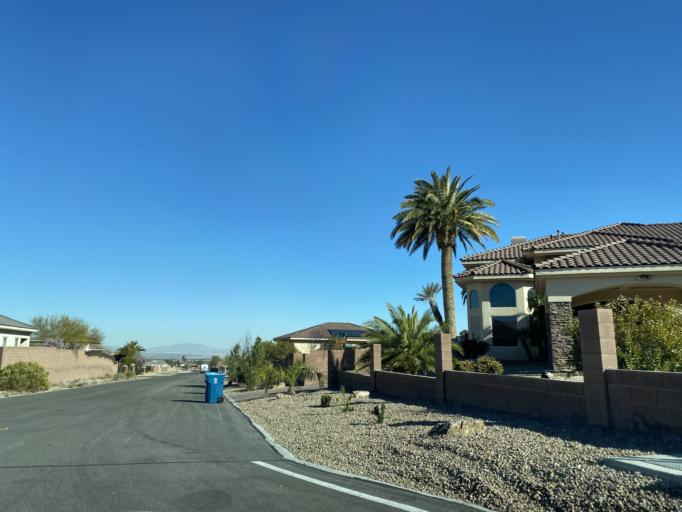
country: US
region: Nevada
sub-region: Clark County
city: Summerlin South
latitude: 36.2935
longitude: -115.3130
